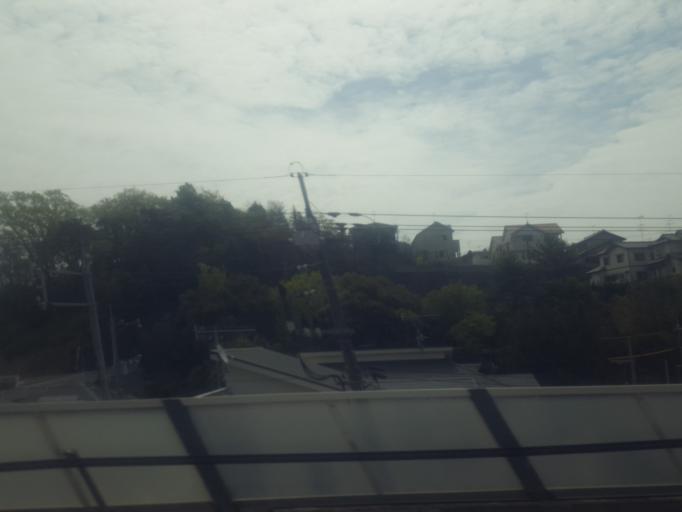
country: JP
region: Hiroshima
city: Miyajima
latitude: 34.3165
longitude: 132.2926
